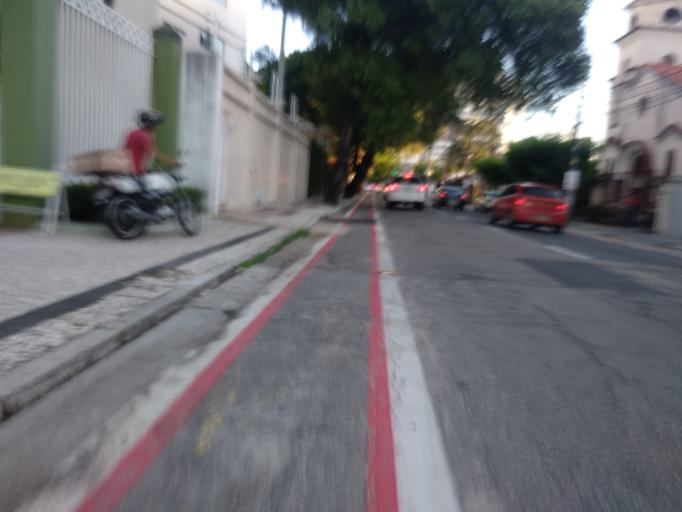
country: BR
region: Ceara
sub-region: Fortaleza
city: Fortaleza
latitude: -3.7335
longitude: -38.5086
